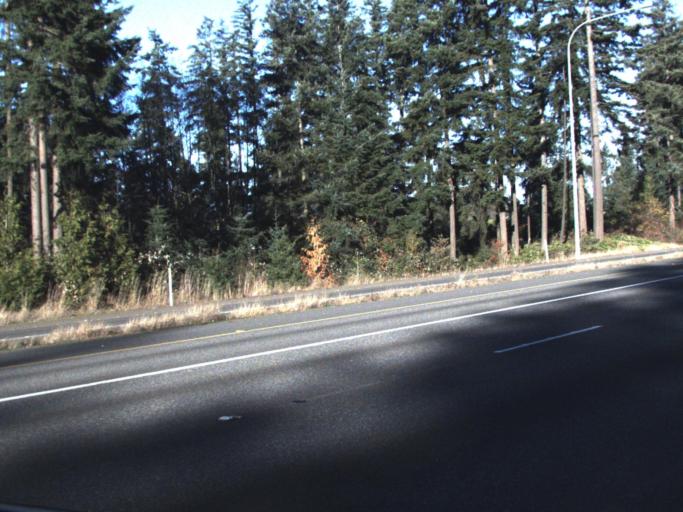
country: US
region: Washington
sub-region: Snohomish County
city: Mill Creek
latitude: 47.9026
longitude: -122.2122
